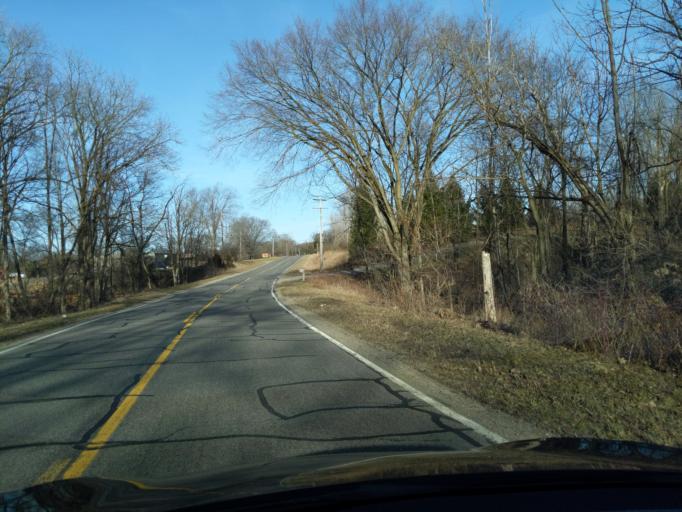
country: US
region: Michigan
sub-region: Ionia County
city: Saranac
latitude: 42.9352
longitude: -85.1937
